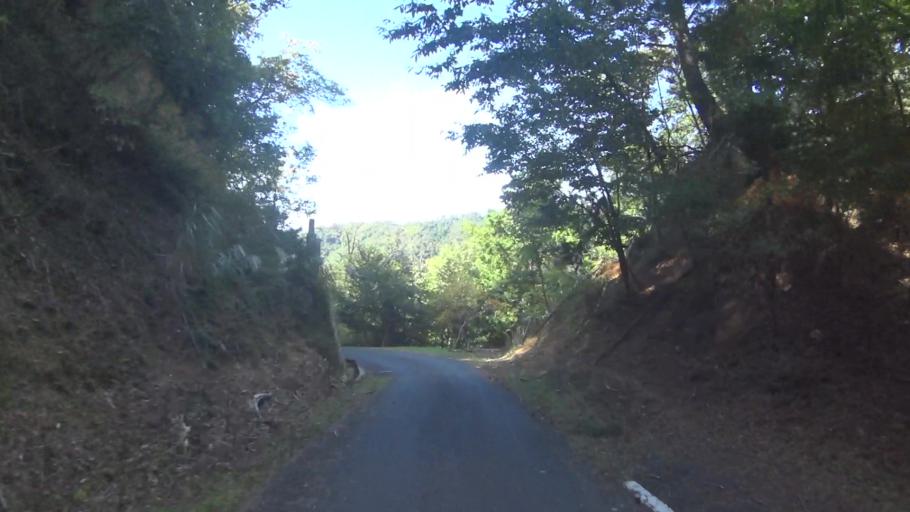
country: JP
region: Hyogo
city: Toyooka
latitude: 35.6068
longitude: 134.9955
